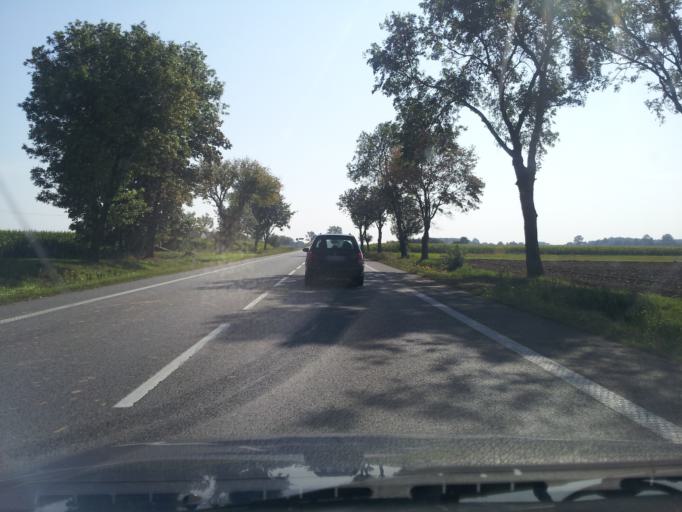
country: PL
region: Masovian Voivodeship
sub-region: Powiat sierpecki
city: Sierpc
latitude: 52.8385
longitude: 19.7332
